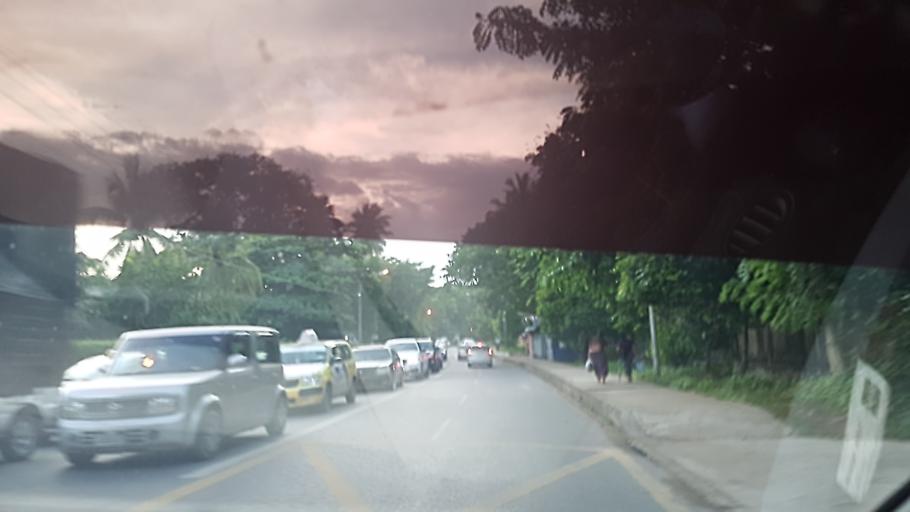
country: MM
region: Yangon
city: Yangon
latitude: 16.8076
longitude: 96.1444
